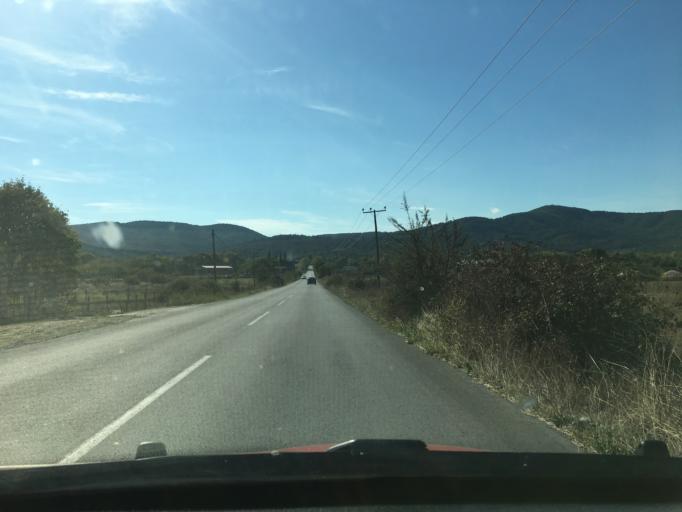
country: GR
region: Central Macedonia
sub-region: Nomos Chalkidikis
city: Ierissos
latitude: 40.3944
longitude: 23.7849
